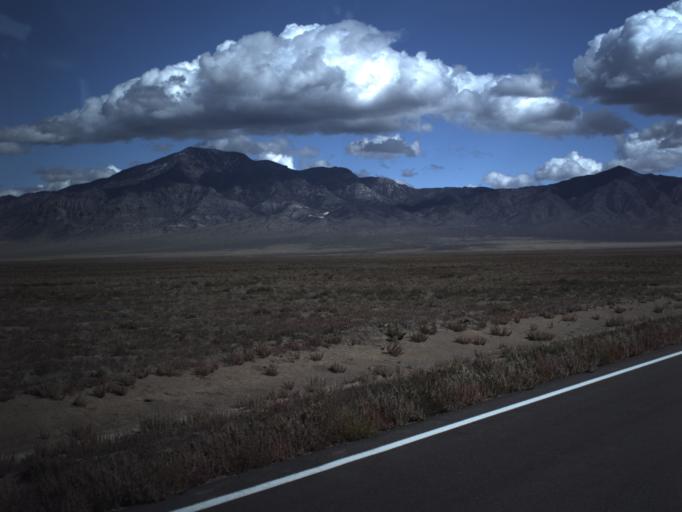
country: US
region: Utah
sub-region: Beaver County
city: Milford
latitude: 38.4736
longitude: -113.4164
